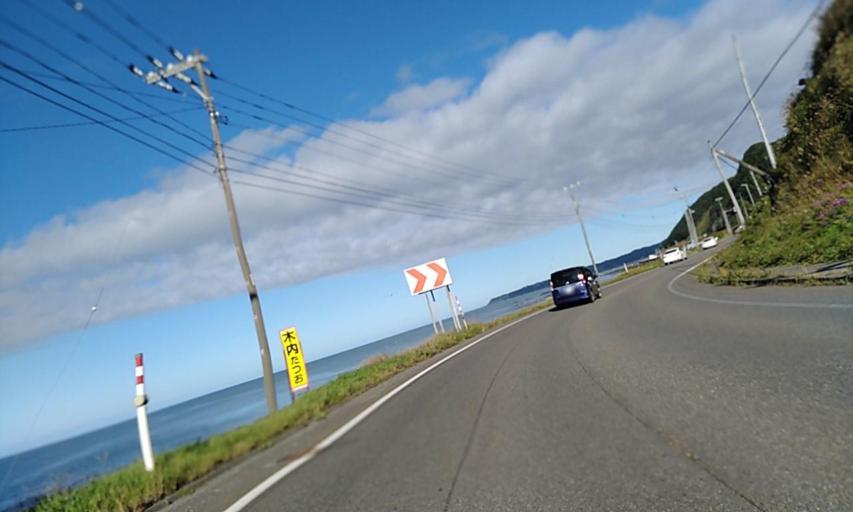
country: JP
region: Hokkaido
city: Shizunai-furukawacho
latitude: 42.2747
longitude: 142.4768
